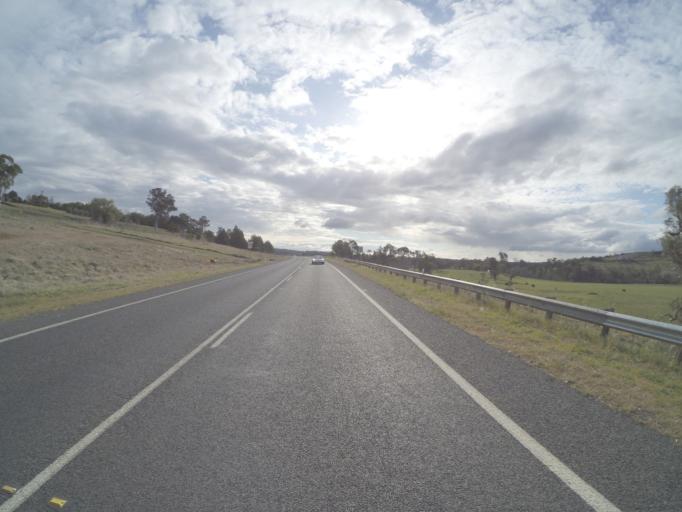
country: AU
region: New South Wales
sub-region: Wingecarribee
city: Bundanoon
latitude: -34.5861
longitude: 150.2617
